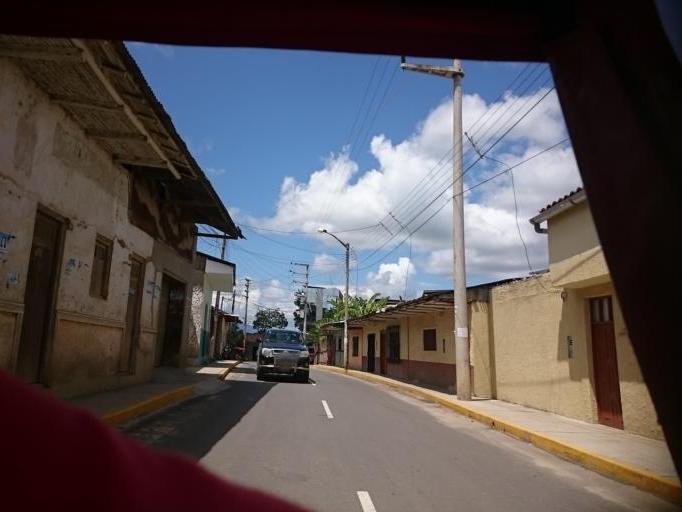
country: PE
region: San Martin
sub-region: Provincia de San Martin
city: Tarapoto
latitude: -6.4847
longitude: -76.3567
